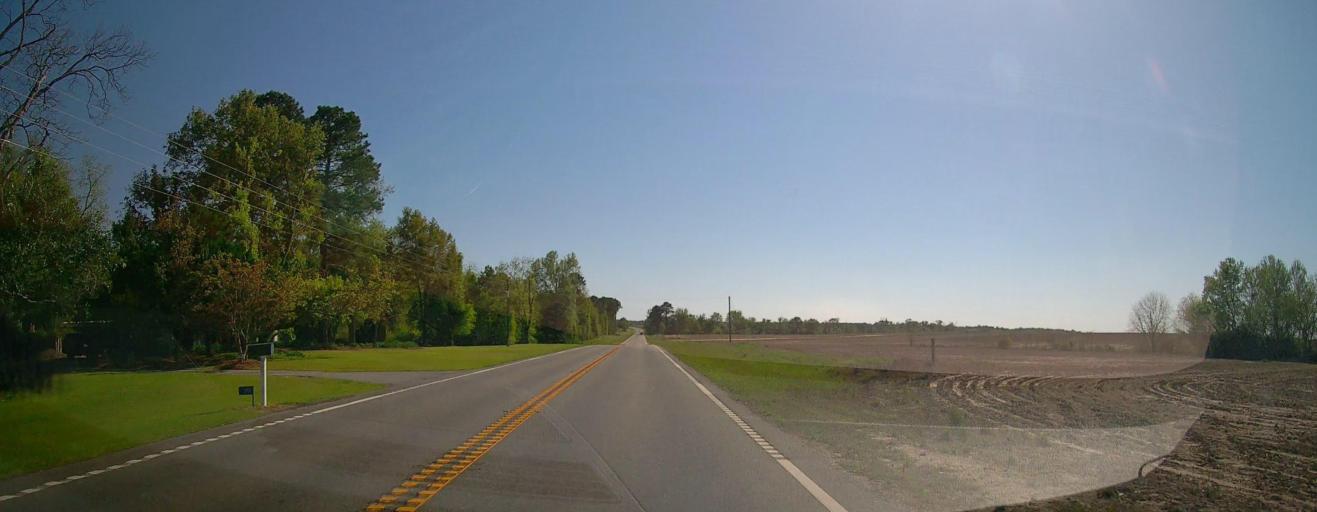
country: US
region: Georgia
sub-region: Pulaski County
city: Hawkinsville
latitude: 32.2134
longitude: -83.4845
